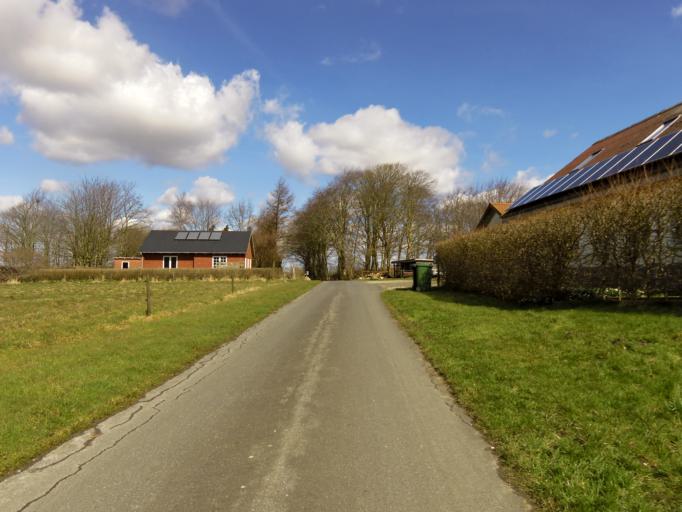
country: DK
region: South Denmark
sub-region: Tonder Kommune
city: Toftlund
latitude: 55.1544
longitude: 9.0383
